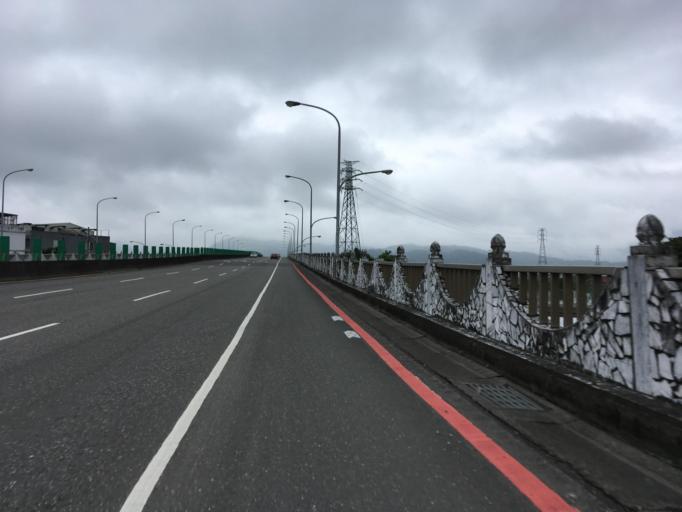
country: TW
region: Taiwan
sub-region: Yilan
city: Yilan
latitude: 24.7743
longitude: 121.7638
